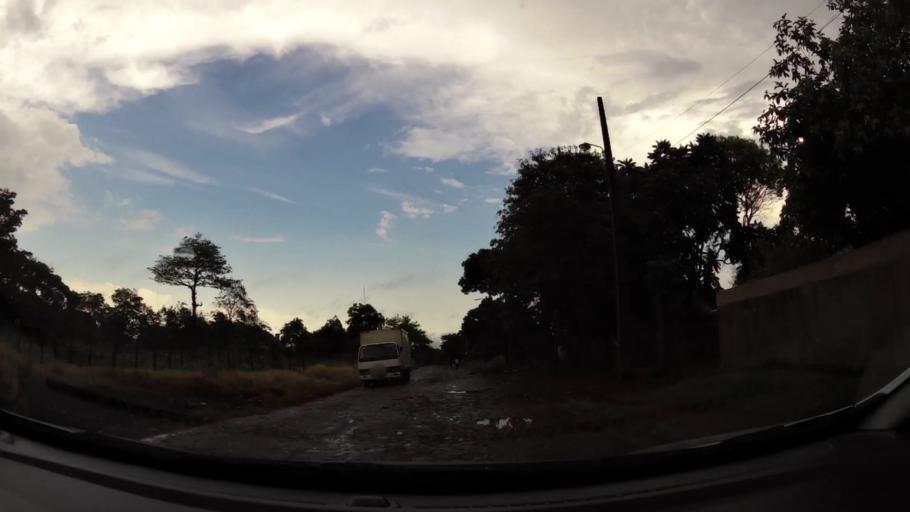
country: PY
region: Alto Parana
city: Presidente Franco
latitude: -25.5373
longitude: -54.6561
